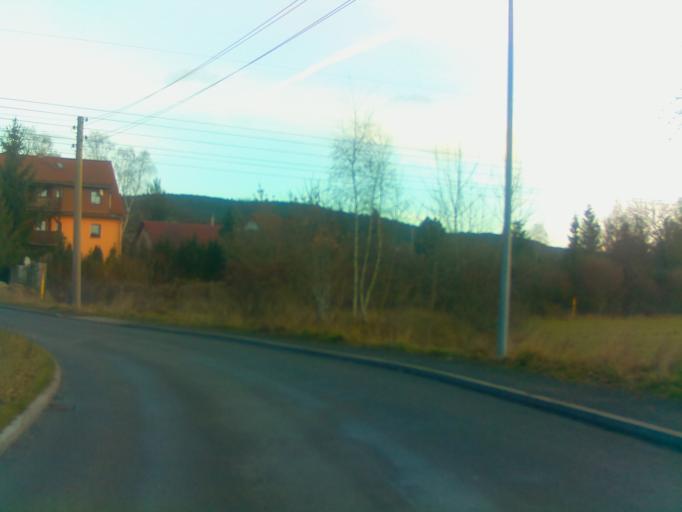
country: DE
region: Thuringia
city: Saalfeld
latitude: 50.6643
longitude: 11.3764
